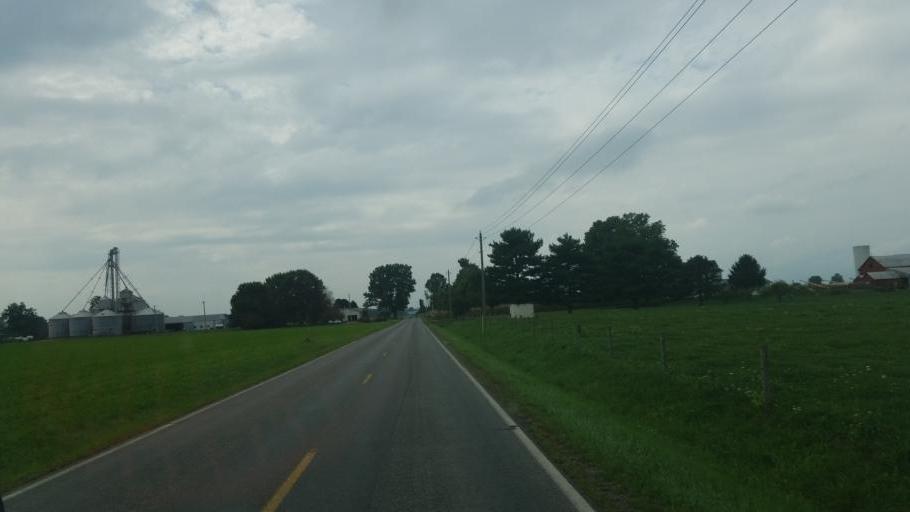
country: US
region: Ohio
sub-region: Wayne County
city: Creston
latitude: 40.9605
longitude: -81.8541
